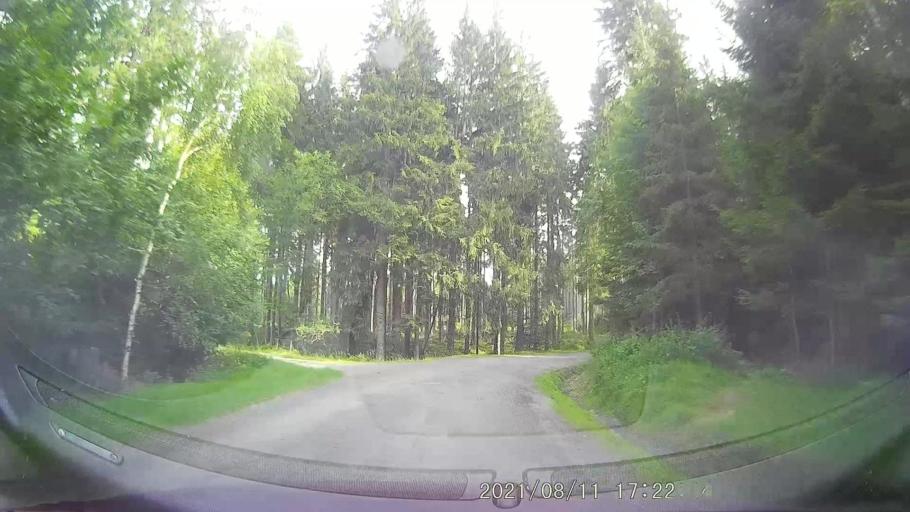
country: PL
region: Lower Silesian Voivodeship
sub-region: Powiat klodzki
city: Polanica-Zdroj
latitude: 50.3072
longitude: 16.5054
